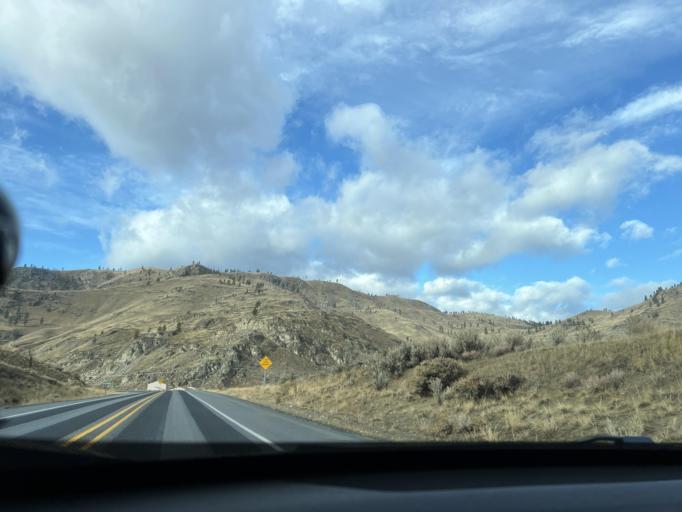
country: US
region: Washington
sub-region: Chelan County
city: Chelan
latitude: 47.8621
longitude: -119.9443
